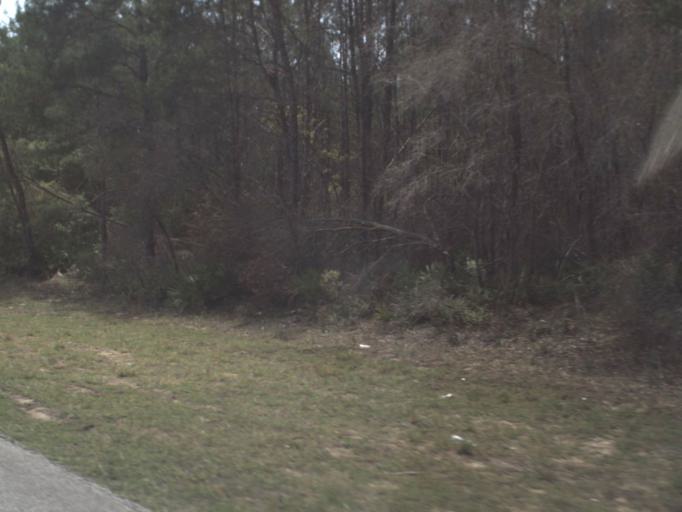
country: US
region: Florida
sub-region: Putnam County
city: Crescent City
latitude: 29.3219
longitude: -81.7009
